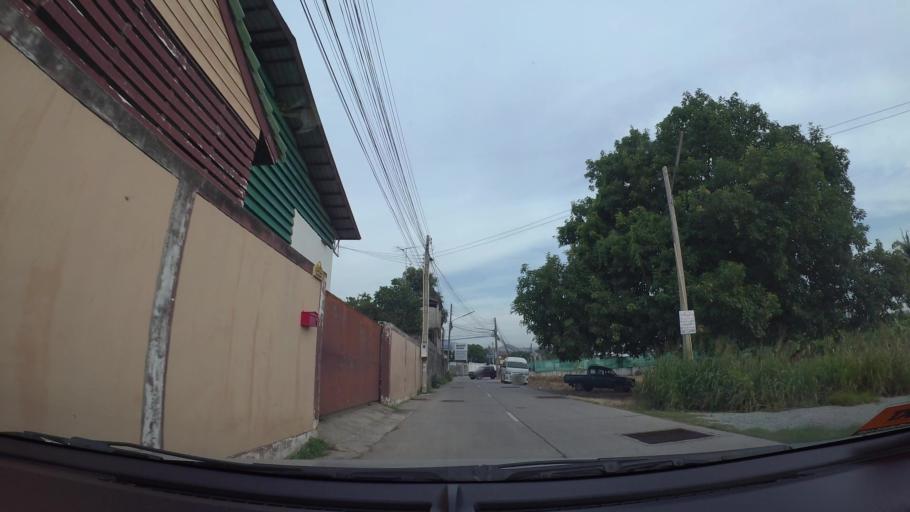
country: TH
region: Chon Buri
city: Chon Buri
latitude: 13.3349
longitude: 100.9784
